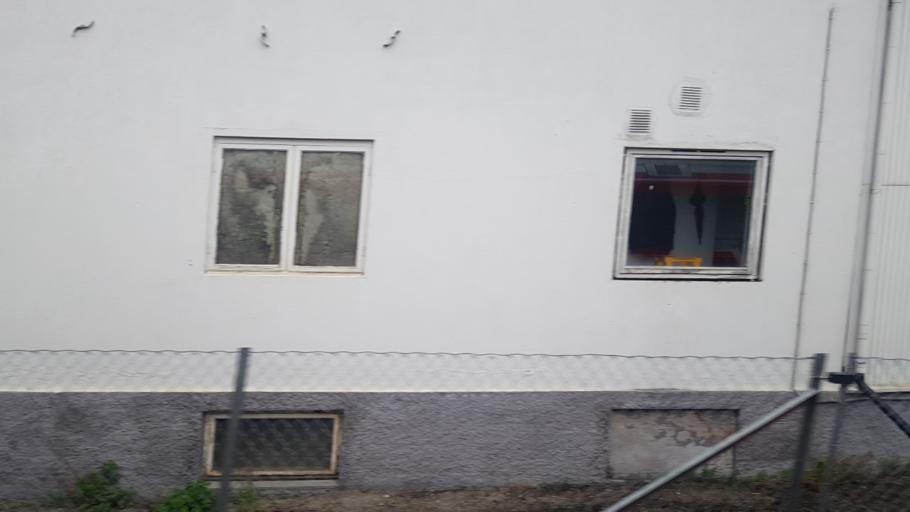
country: NO
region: Oppland
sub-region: Nord-Fron
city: Vinstra
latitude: 61.5953
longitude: 9.7341
